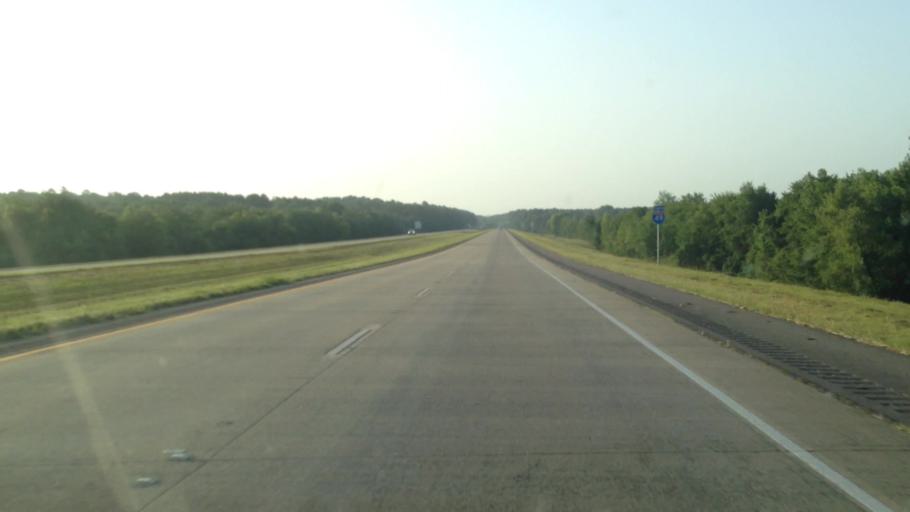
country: US
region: Louisiana
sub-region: Grant Parish
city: Colfax
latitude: 31.4883
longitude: -92.8534
